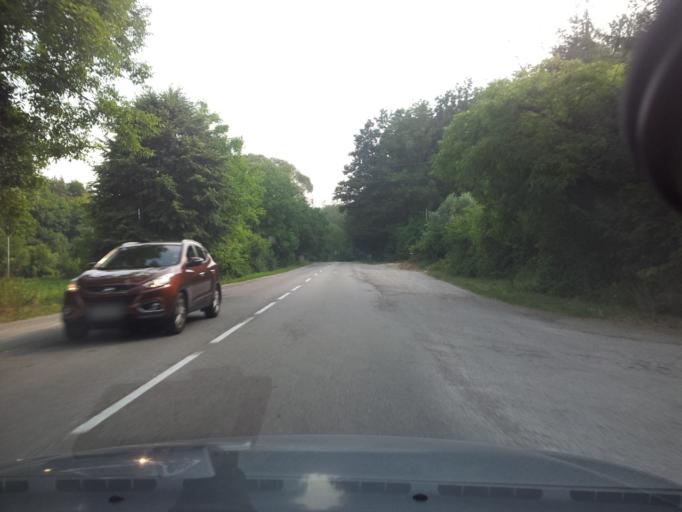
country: SK
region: Nitriansky
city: Trencianske Teplice
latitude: 48.8521
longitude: 18.1834
